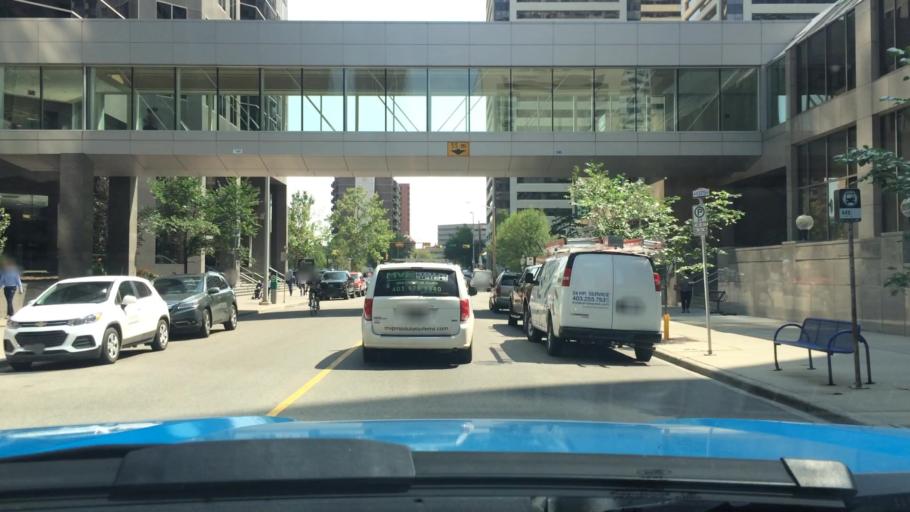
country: CA
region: Alberta
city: Calgary
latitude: 51.0505
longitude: -114.0674
